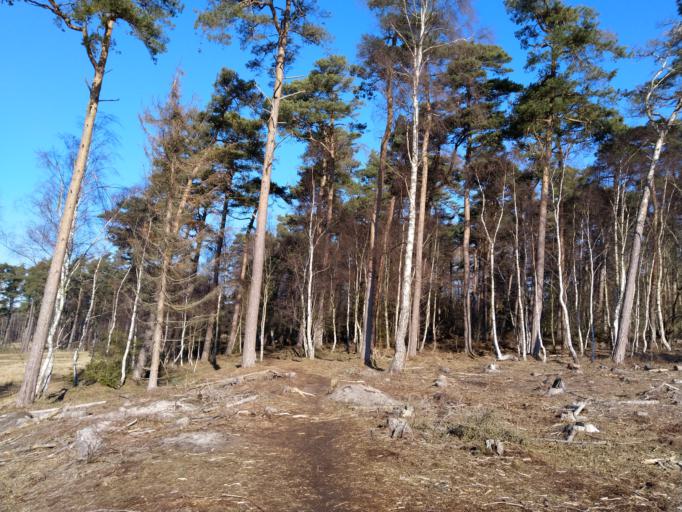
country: DK
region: Zealand
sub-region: Guldborgsund Kommune
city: Nykobing Falster
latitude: 54.6415
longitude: 11.9574
